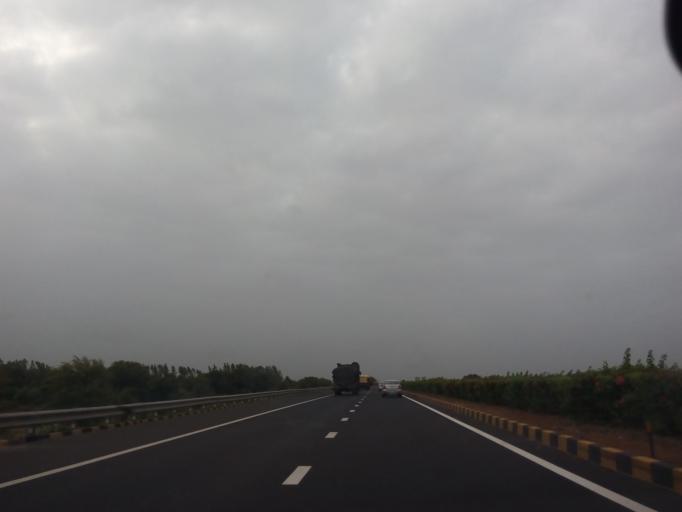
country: IN
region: Gujarat
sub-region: Anand
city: Anand
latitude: 22.6050
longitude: 72.9740
